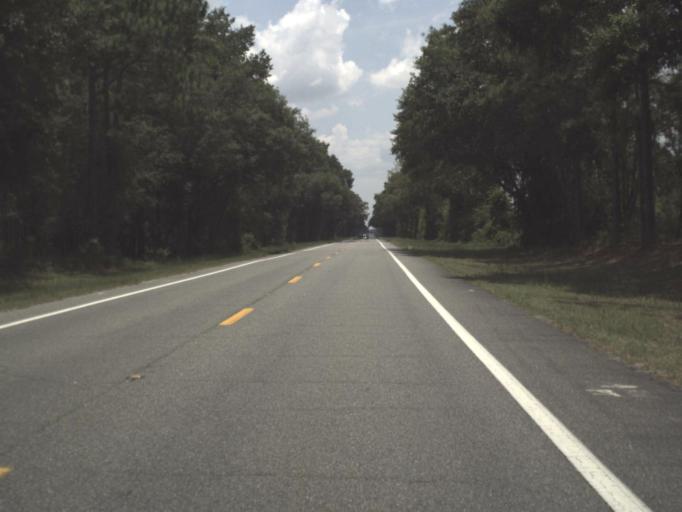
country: US
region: Florida
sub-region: Madison County
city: Madison
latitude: 30.4867
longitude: -83.2288
